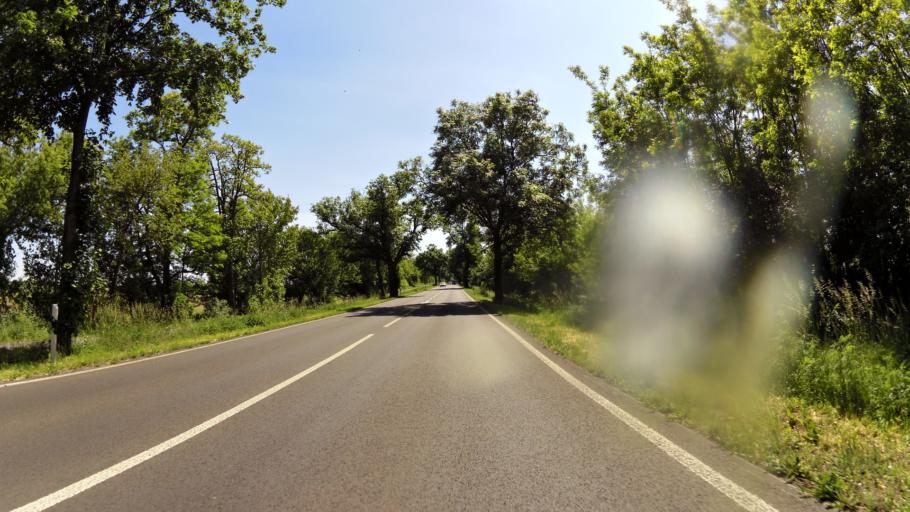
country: DE
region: Brandenburg
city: Lebus
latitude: 52.3864
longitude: 14.5179
